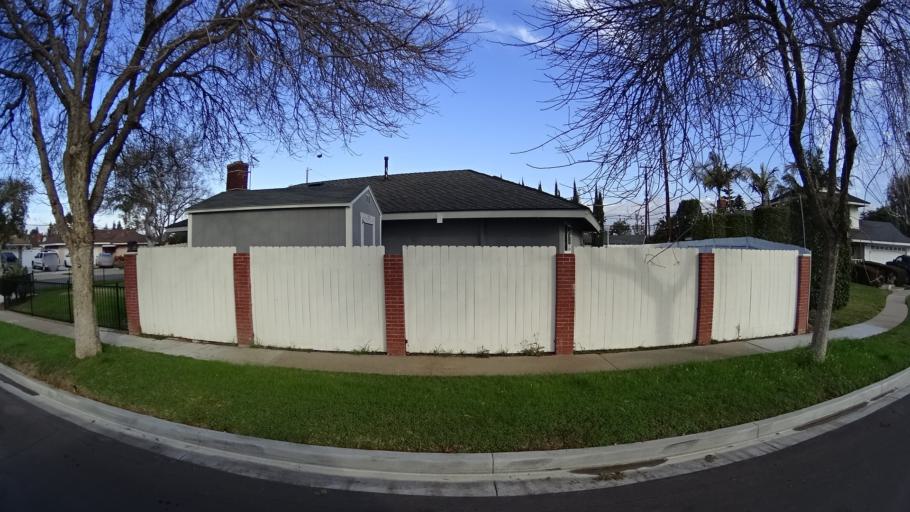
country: US
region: California
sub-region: Orange County
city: Yorba Linda
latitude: 33.8539
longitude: -117.8116
